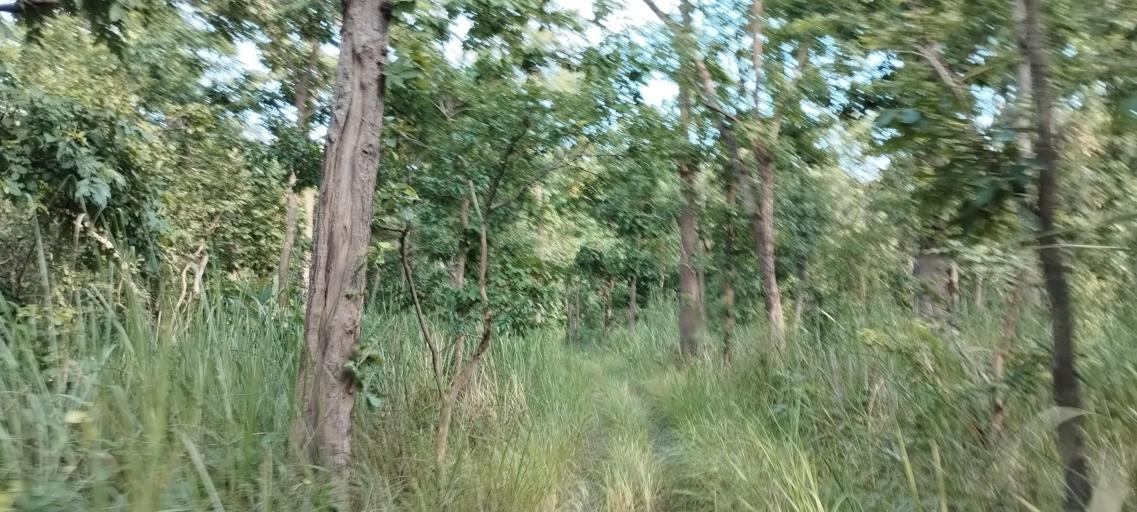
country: NP
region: Far Western
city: Tikapur
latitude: 28.5509
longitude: 81.2849
